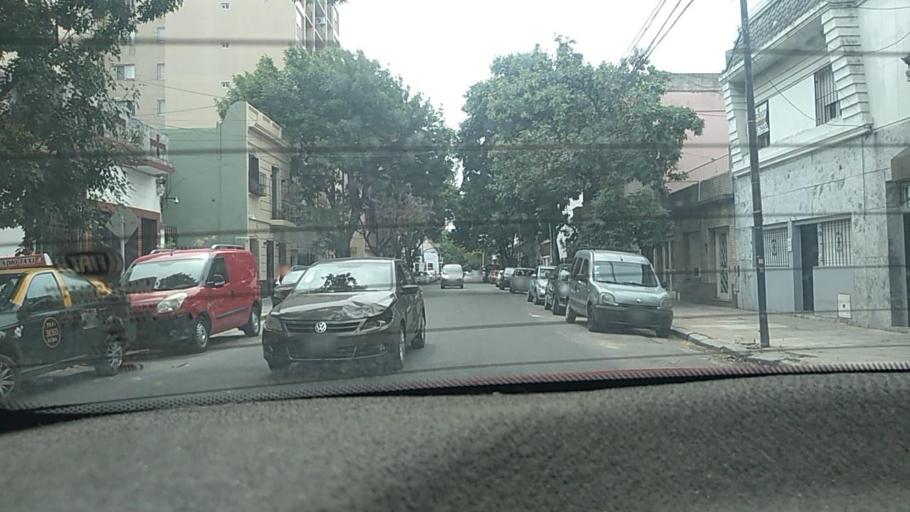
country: AR
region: Buenos Aires F.D.
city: Villa Santa Rita
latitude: -34.6339
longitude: -58.4782
